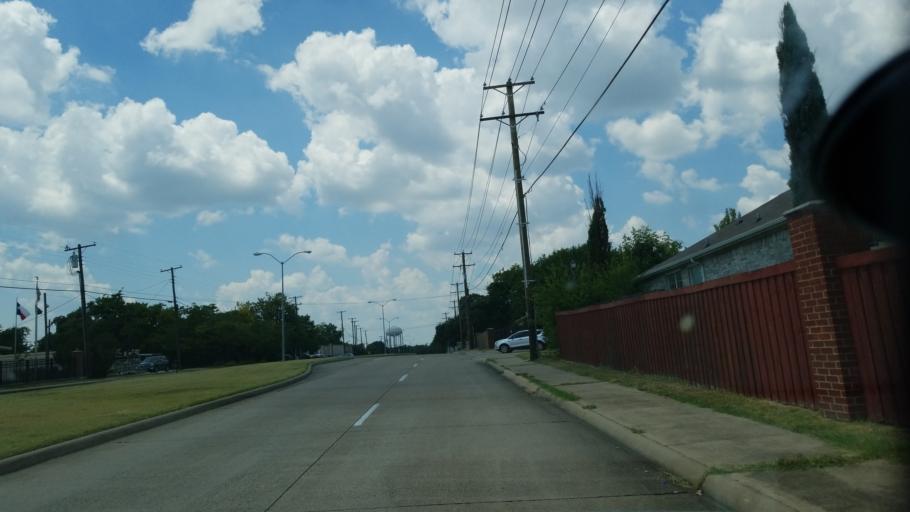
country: US
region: Texas
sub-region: Dallas County
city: Duncanville
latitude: 32.6767
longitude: -96.8973
